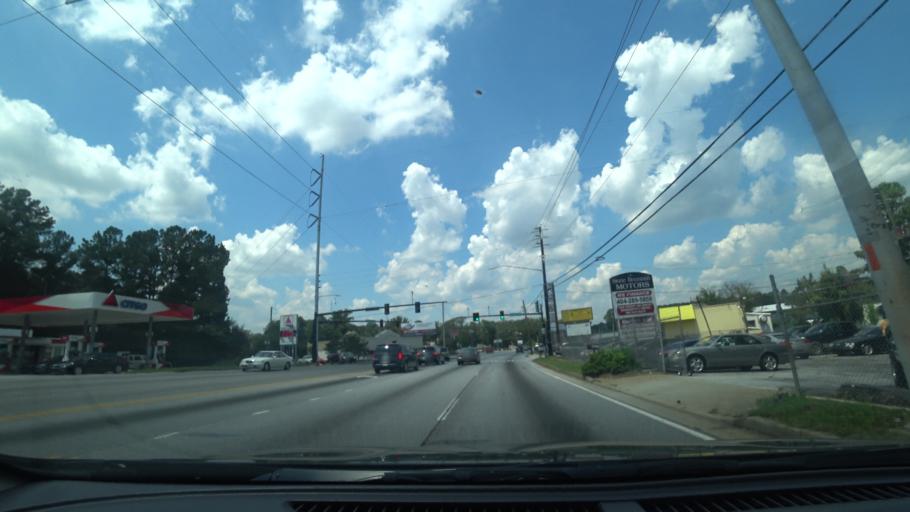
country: US
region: Georgia
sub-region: DeKalb County
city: Belvedere Park
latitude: 33.7365
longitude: -84.2164
